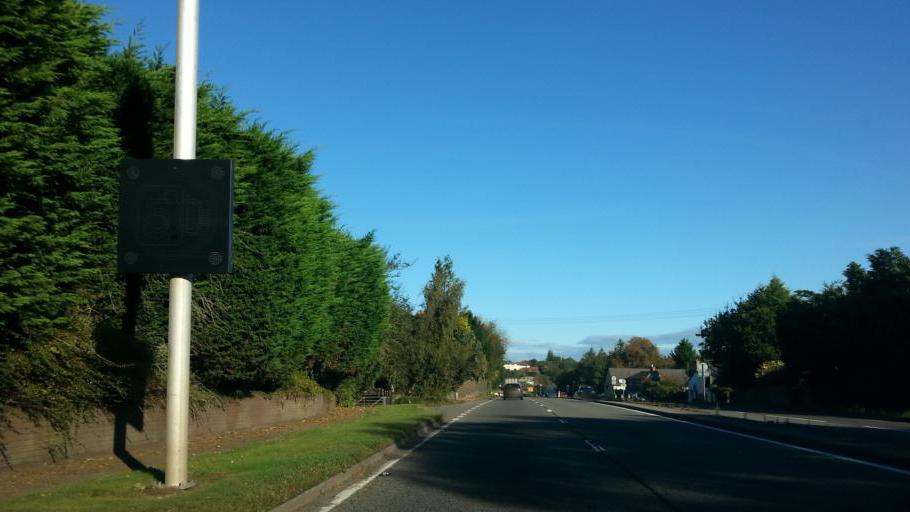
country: GB
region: England
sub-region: Herefordshire
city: Marstow
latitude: 51.8836
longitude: -2.6335
